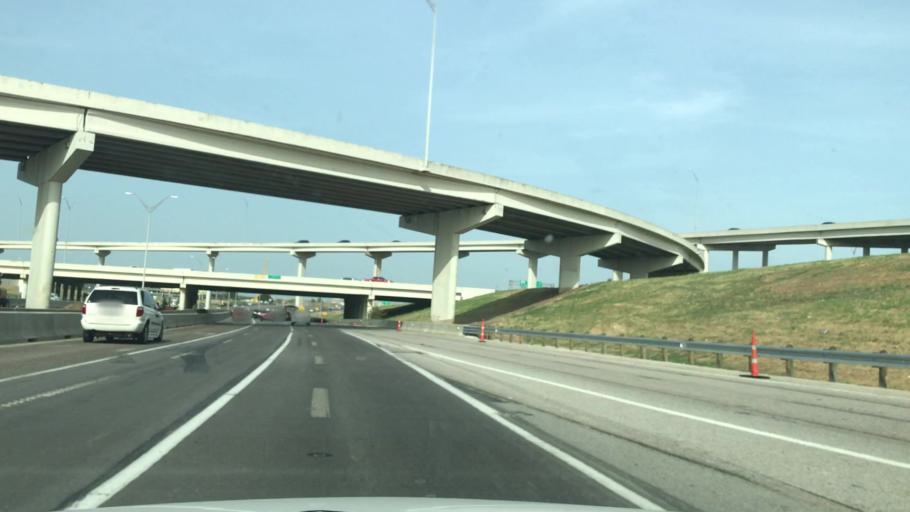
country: US
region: Texas
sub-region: Tarrant County
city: Euless
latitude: 32.8387
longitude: -97.0593
